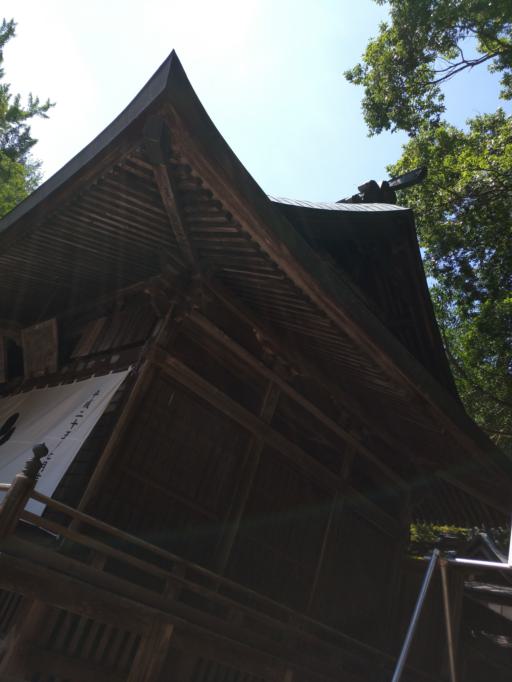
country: JP
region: Tochigi
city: Kuroiso
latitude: 37.1128
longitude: 140.2192
